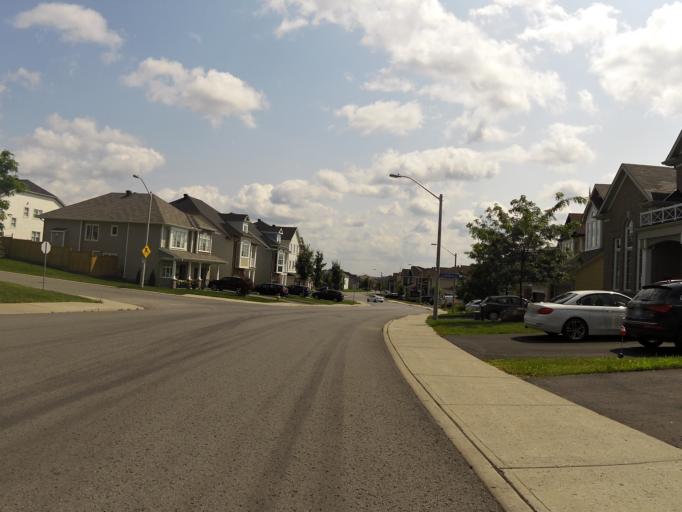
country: CA
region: Ontario
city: Bells Corners
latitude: 45.3153
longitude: -75.9352
